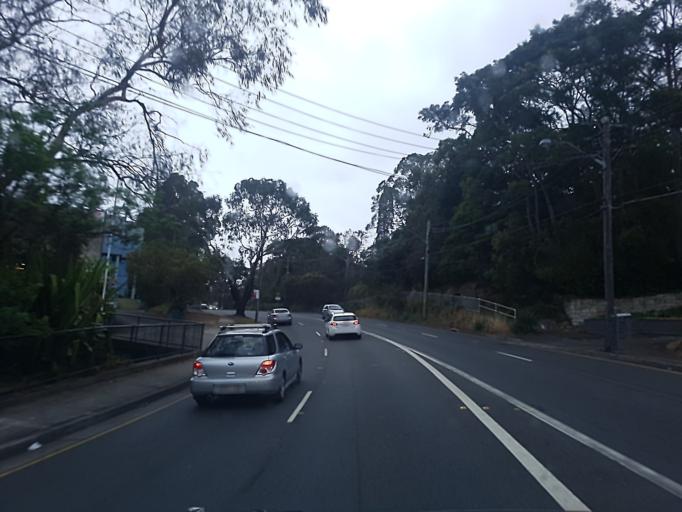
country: AU
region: New South Wales
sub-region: Ku-ring-gai
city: Roseville Chase
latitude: -33.7849
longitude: 151.2004
